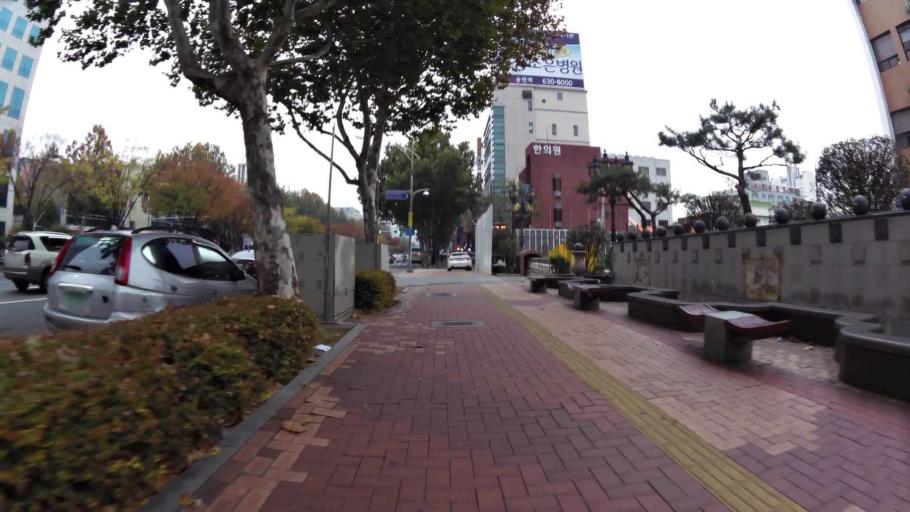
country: KR
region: Daegu
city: Daegu
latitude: 35.8586
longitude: 128.6318
